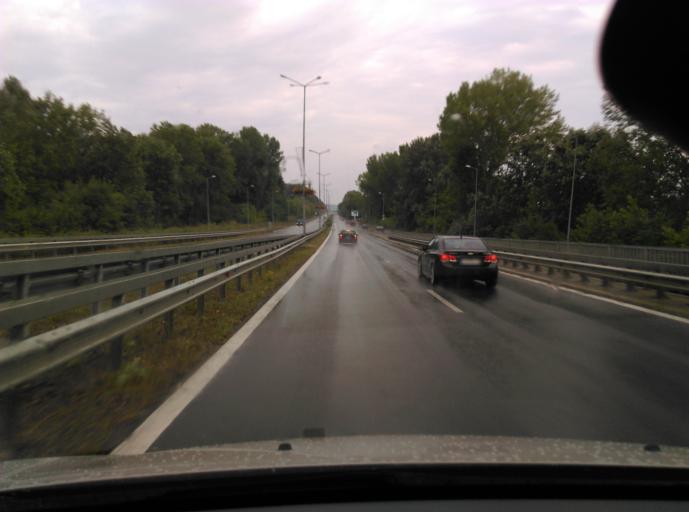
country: BG
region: Burgas
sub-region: Obshtina Burgas
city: Burgas
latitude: 42.4715
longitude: 27.4361
